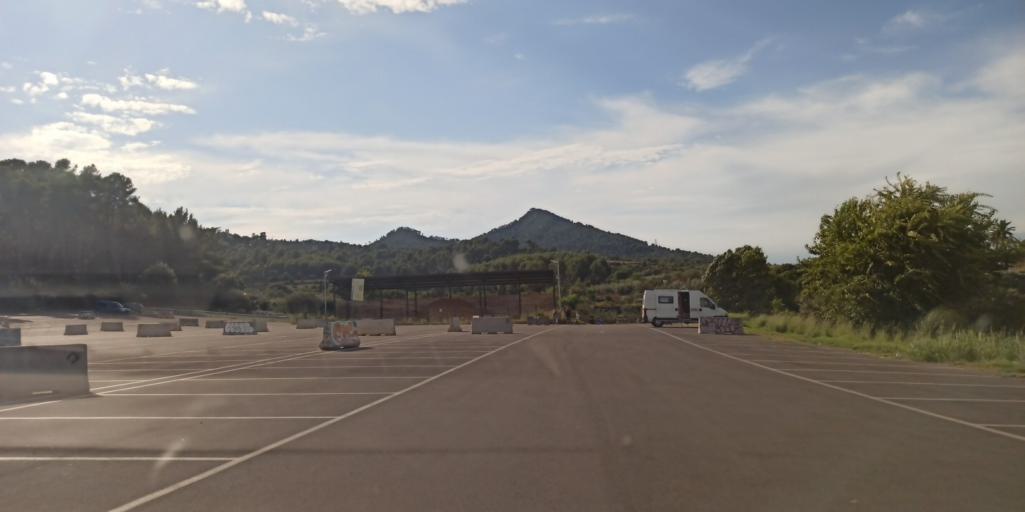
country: ES
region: Catalonia
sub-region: Provincia de Barcelona
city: Santa Coloma de Cervello
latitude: 41.3558
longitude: 2.0225
